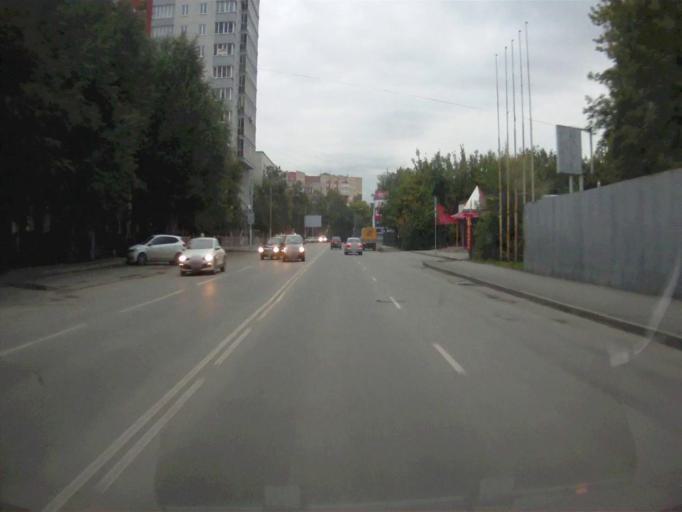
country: RU
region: Chelyabinsk
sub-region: Gorod Chelyabinsk
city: Chelyabinsk
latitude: 55.1519
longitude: 61.3984
